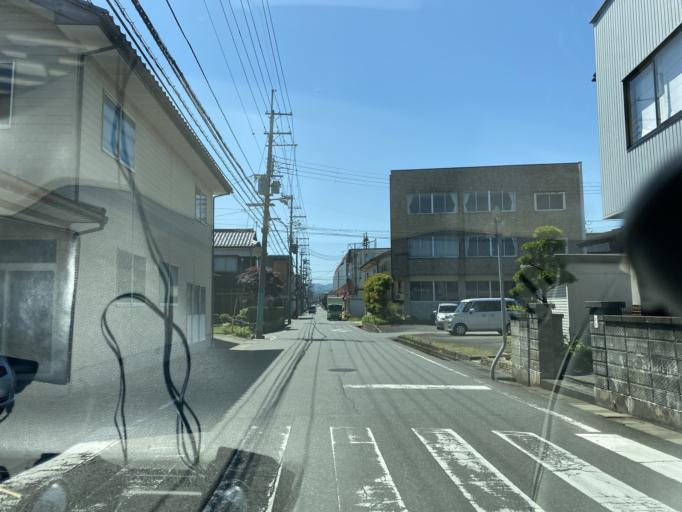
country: JP
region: Hyogo
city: Toyooka
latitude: 35.5369
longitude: 134.8199
